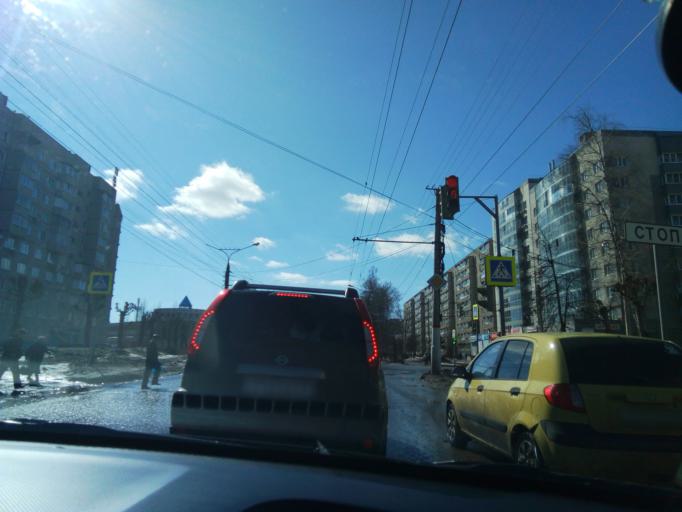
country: RU
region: Chuvashia
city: Novyye Lapsary
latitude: 56.1128
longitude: 47.1852
